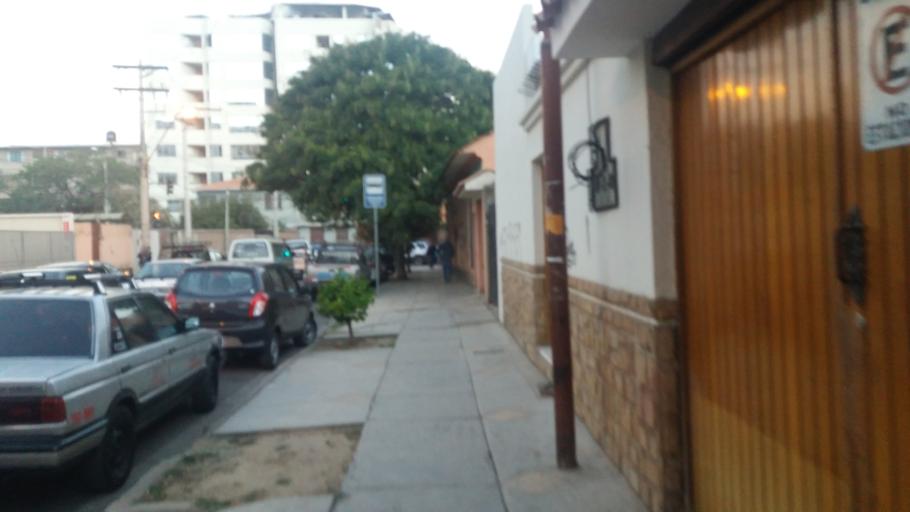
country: BO
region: Cochabamba
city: Cochabamba
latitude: -17.3859
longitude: -66.1525
